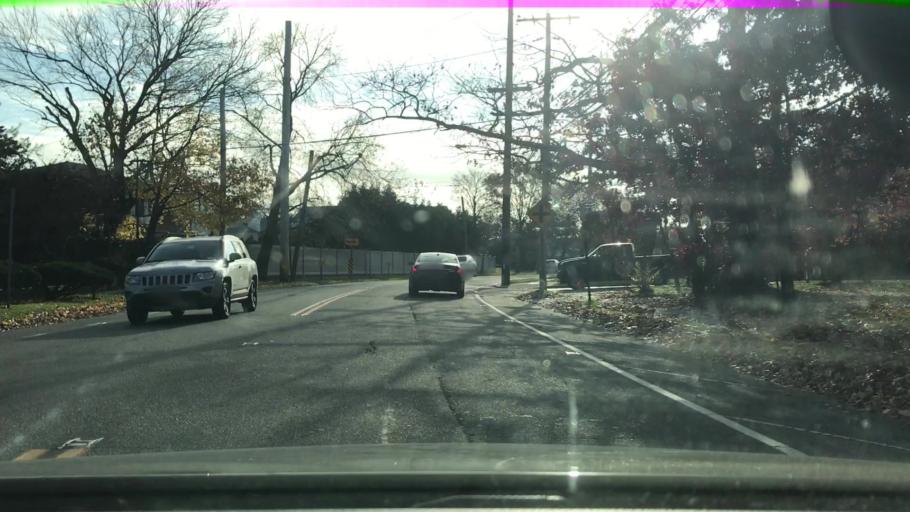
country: US
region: New York
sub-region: Nassau County
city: Cedarhurst
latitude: 40.6219
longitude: -73.7185
